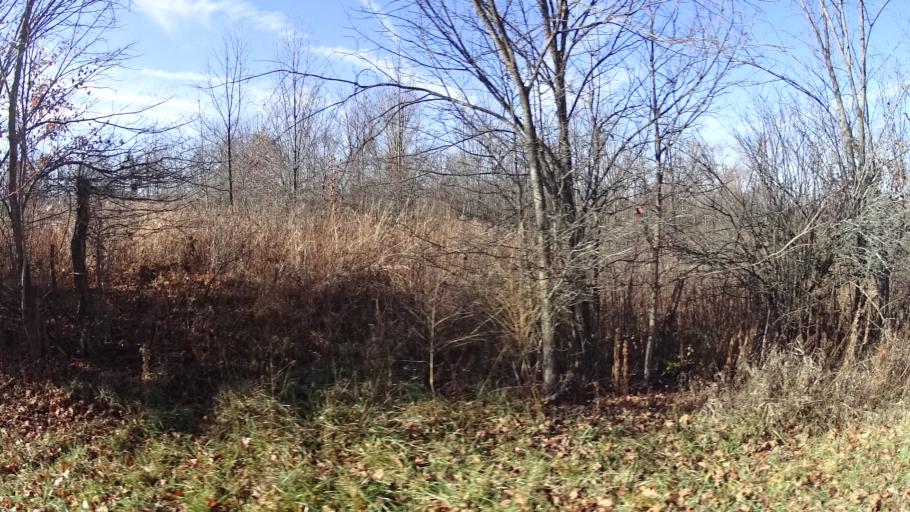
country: US
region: Ohio
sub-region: Lorain County
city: Wellington
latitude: 41.0681
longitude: -82.2796
